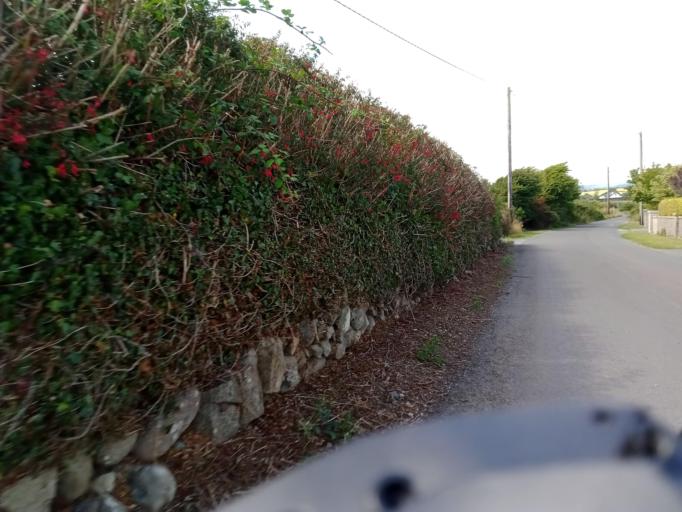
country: IE
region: Munster
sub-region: Waterford
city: Dungarvan
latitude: 52.1284
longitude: -7.4527
